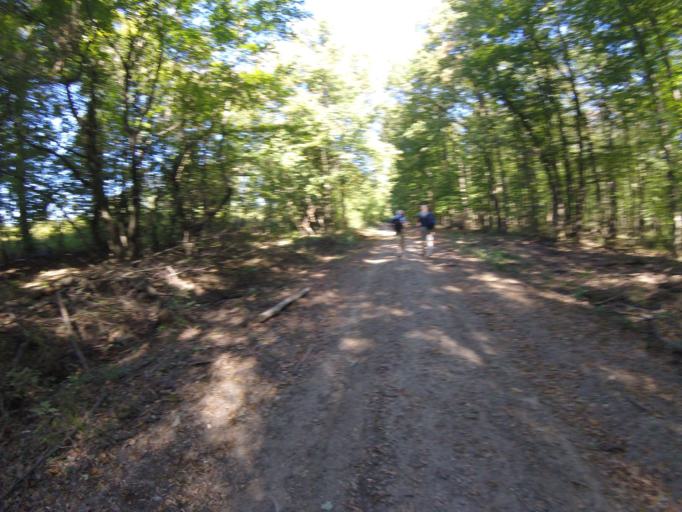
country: HU
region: Komarom-Esztergom
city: Kesztolc
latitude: 47.7641
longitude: 18.8135
